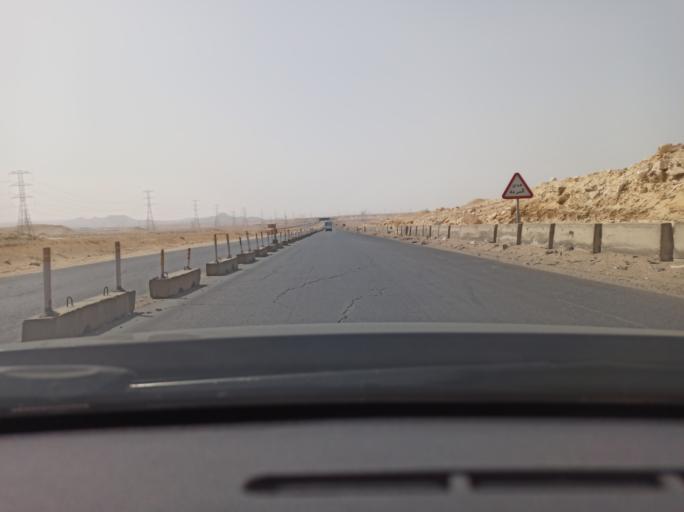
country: EG
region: Muhafazat Bani Suwayf
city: Bush
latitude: 29.1722
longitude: 31.2424
